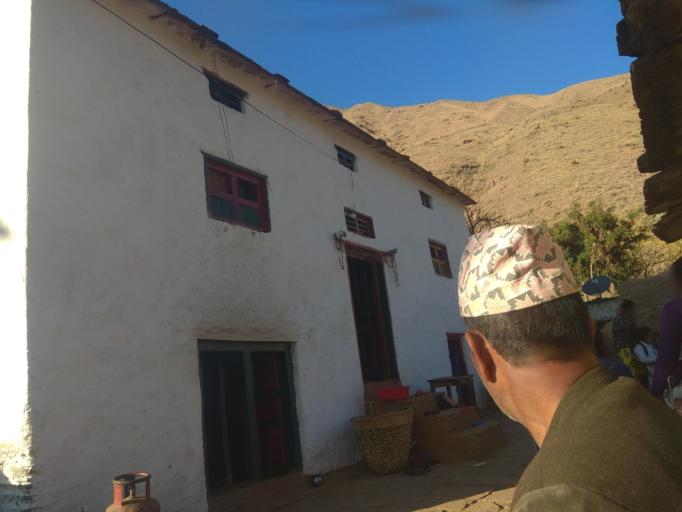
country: NP
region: Mid Western
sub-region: Bheri Zone
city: Dailekh
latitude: 29.2605
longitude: 81.6811
